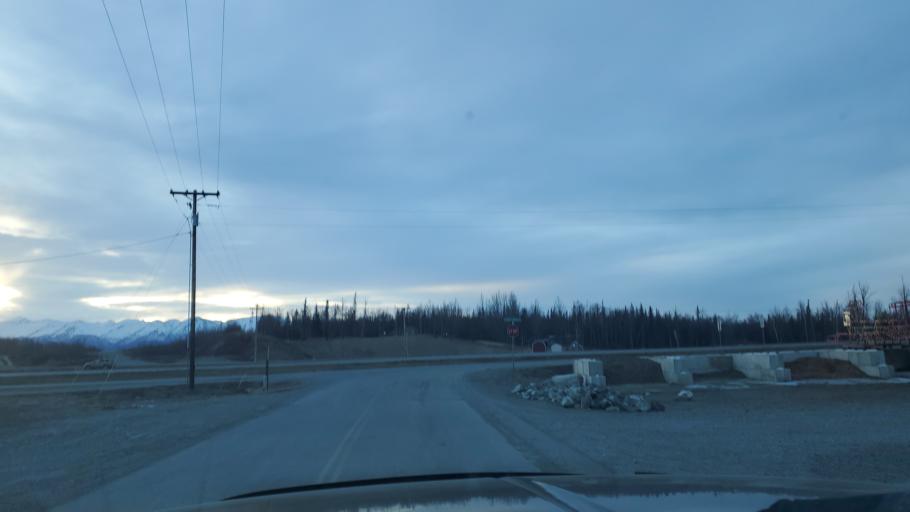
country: US
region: Alaska
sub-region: Matanuska-Susitna Borough
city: Lakes
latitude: 61.5709
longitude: -149.3449
